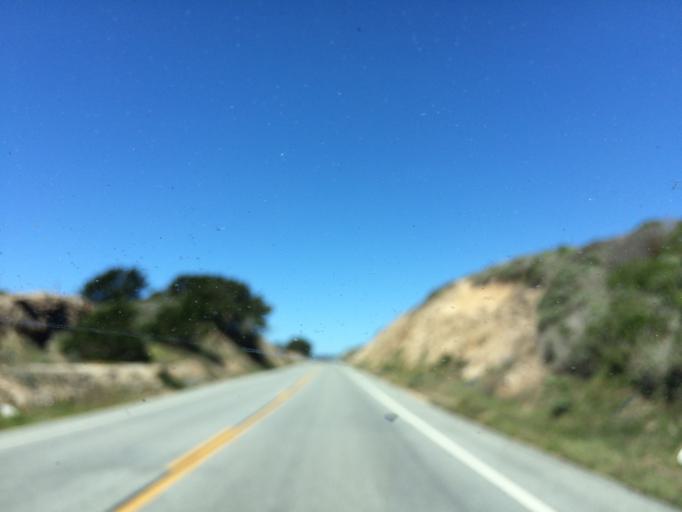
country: US
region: California
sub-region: Santa Cruz County
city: Bonny Doon
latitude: 37.0654
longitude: -122.2542
